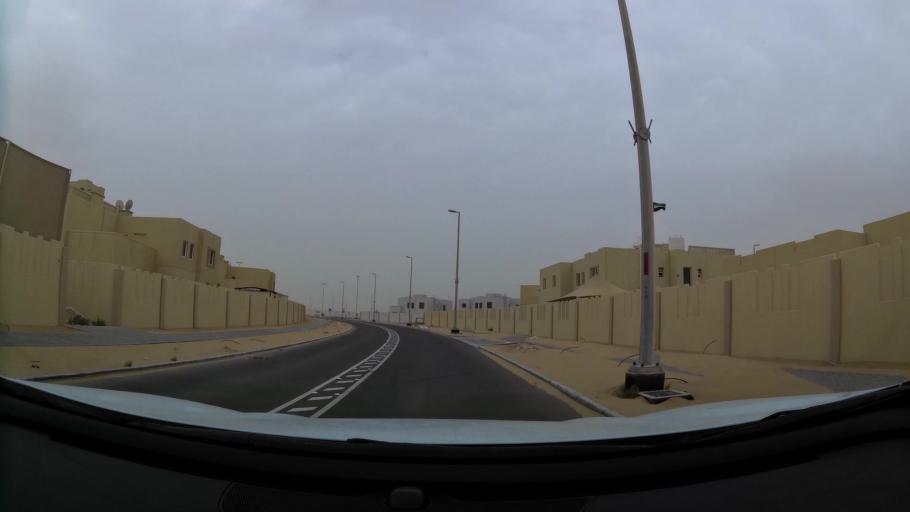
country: AE
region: Abu Dhabi
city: Abu Dhabi
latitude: 24.4369
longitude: 54.7288
